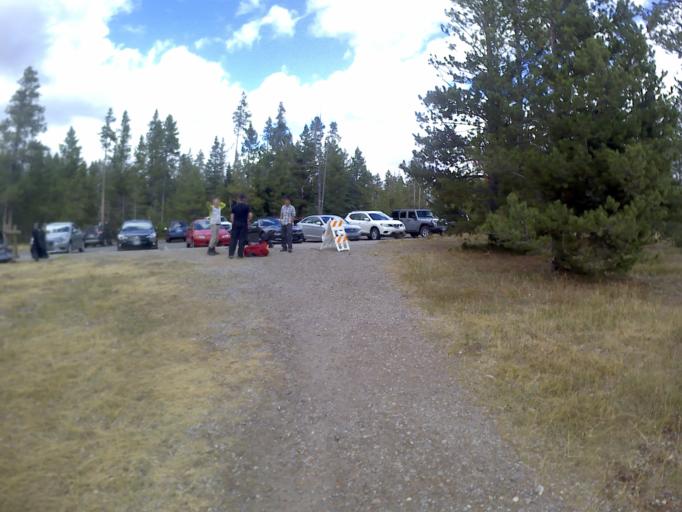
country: US
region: Wyoming
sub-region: Teton County
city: Moose Wilson Road
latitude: 43.7846
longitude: -110.7274
